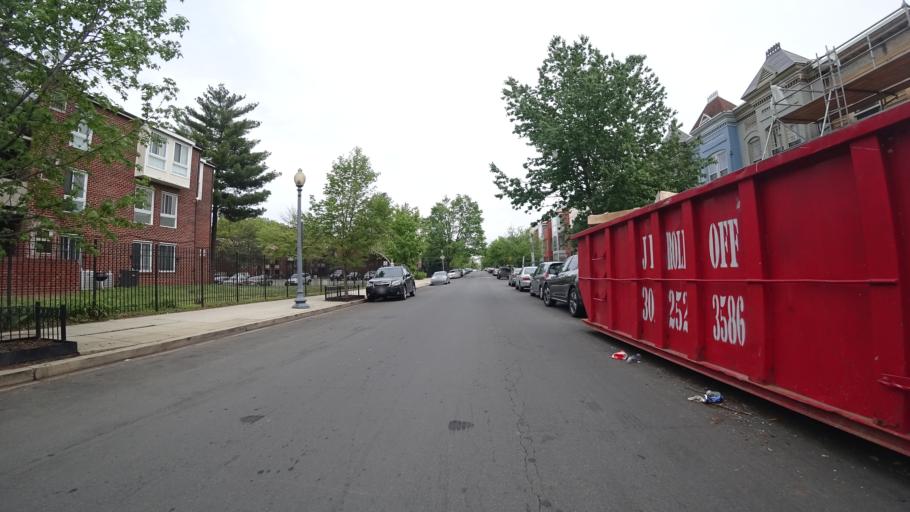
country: US
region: Washington, D.C.
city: Washington, D.C.
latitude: 38.9072
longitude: -77.0180
